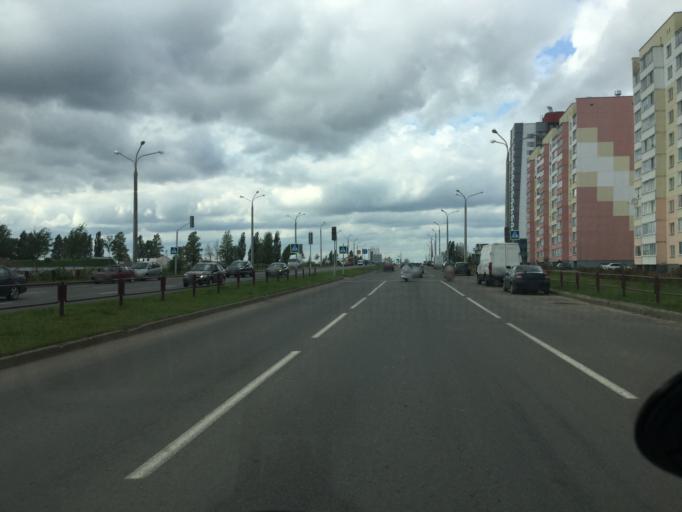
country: BY
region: Vitebsk
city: Vitebsk
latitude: 55.1657
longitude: 30.2613
